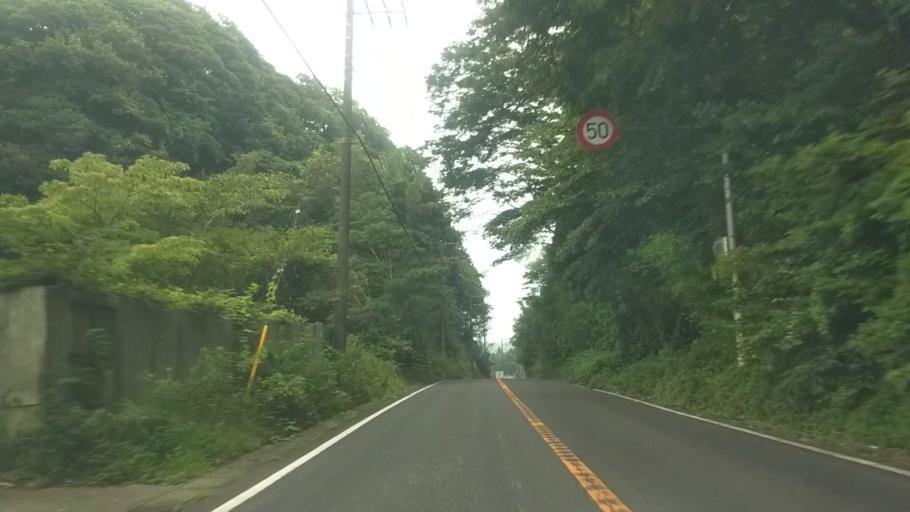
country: JP
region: Chiba
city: Kawaguchi
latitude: 35.2319
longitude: 140.0739
